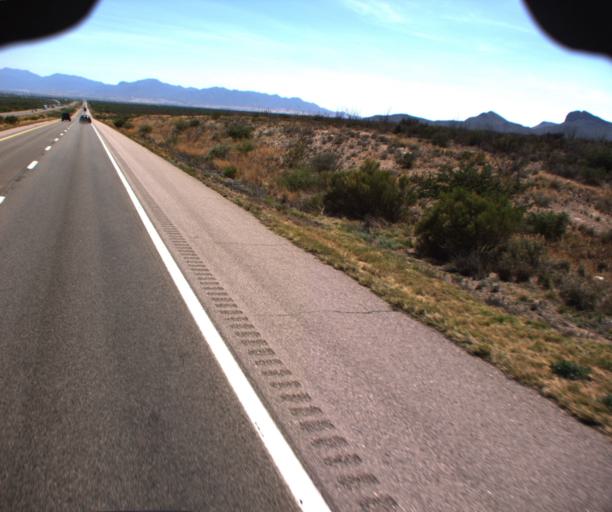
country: US
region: Arizona
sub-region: Cochise County
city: Huachuca City
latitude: 31.7608
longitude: -110.3503
